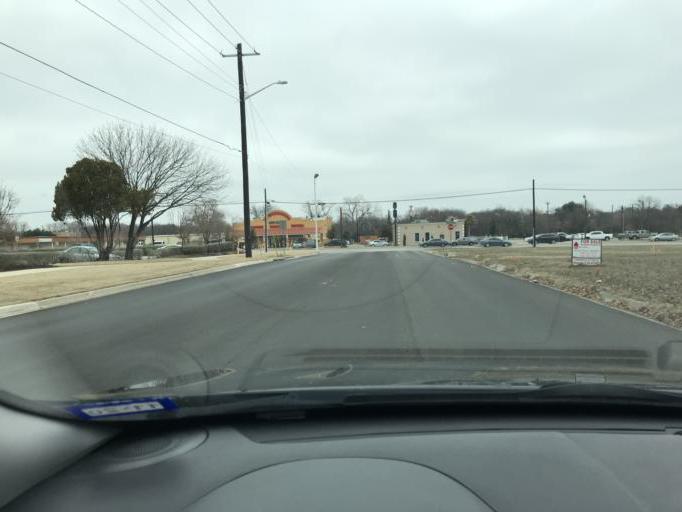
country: US
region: Texas
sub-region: Denton County
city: Denton
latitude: 33.2285
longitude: -97.1551
